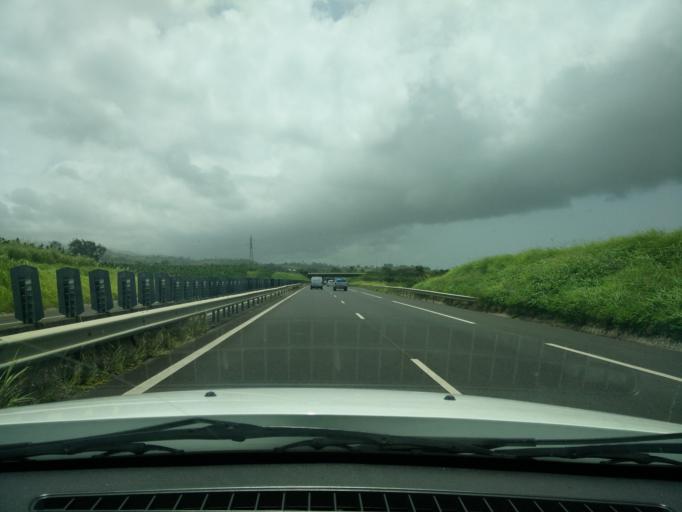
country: GP
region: Guadeloupe
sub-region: Guadeloupe
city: Capesterre-Belle-Eau
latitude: 16.0381
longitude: -61.5747
